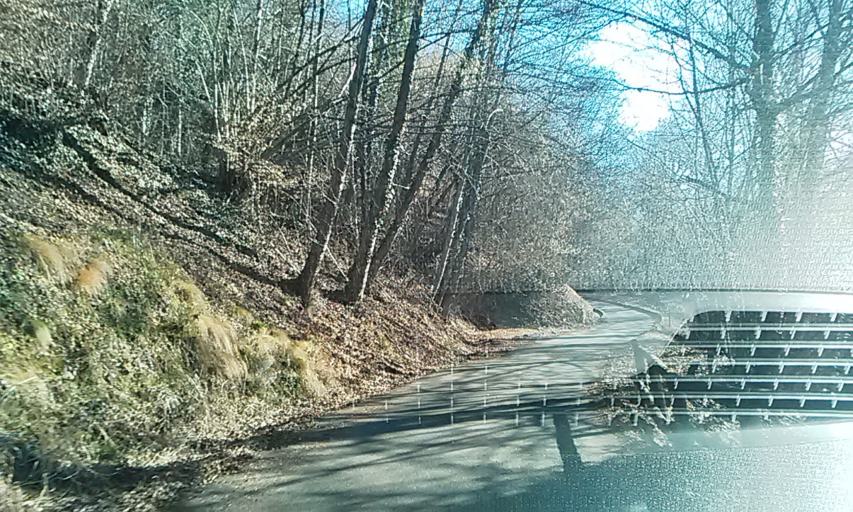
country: IT
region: Piedmont
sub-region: Provincia di Vercelli
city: Guardabosone
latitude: 45.7002
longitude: 8.2448
